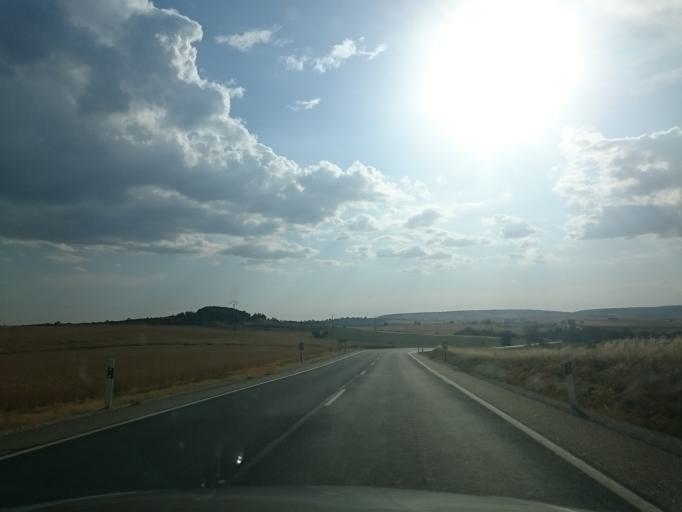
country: ES
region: Castille and Leon
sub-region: Provincia de Burgos
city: Arlanzon
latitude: 42.3487
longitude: -3.4489
